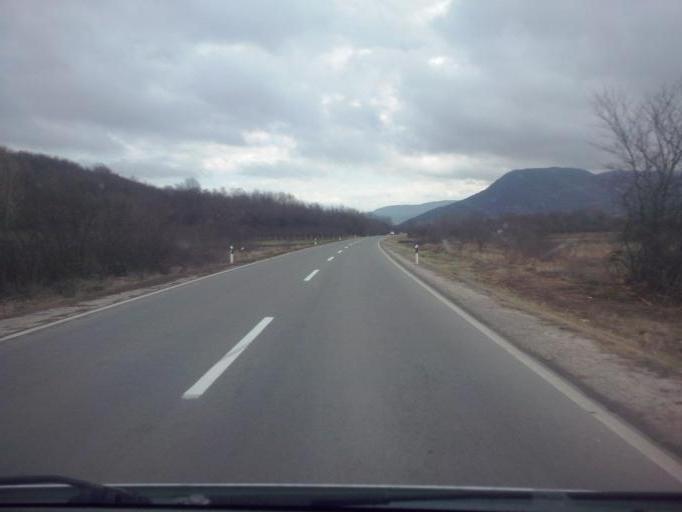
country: RS
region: Central Serbia
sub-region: Pomoravski Okrug
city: Paracin
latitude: 43.8660
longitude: 21.4935
